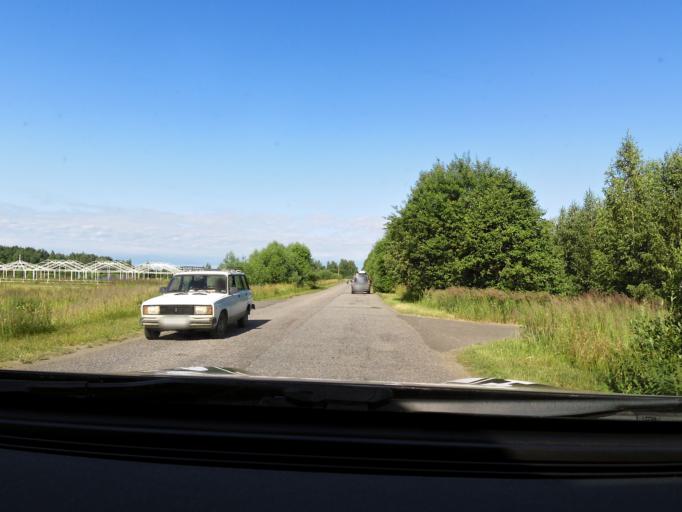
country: RU
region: Tverskaya
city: Zavidovo
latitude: 56.6090
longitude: 36.5673
